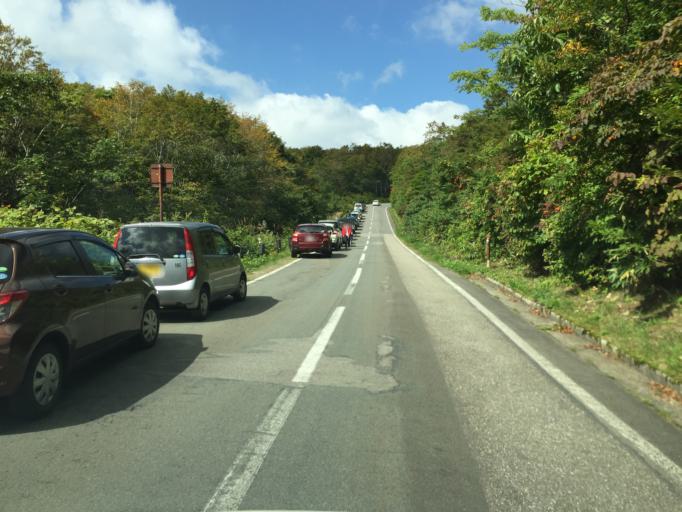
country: JP
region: Fukushima
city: Inawashiro
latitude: 37.6118
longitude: 140.0495
